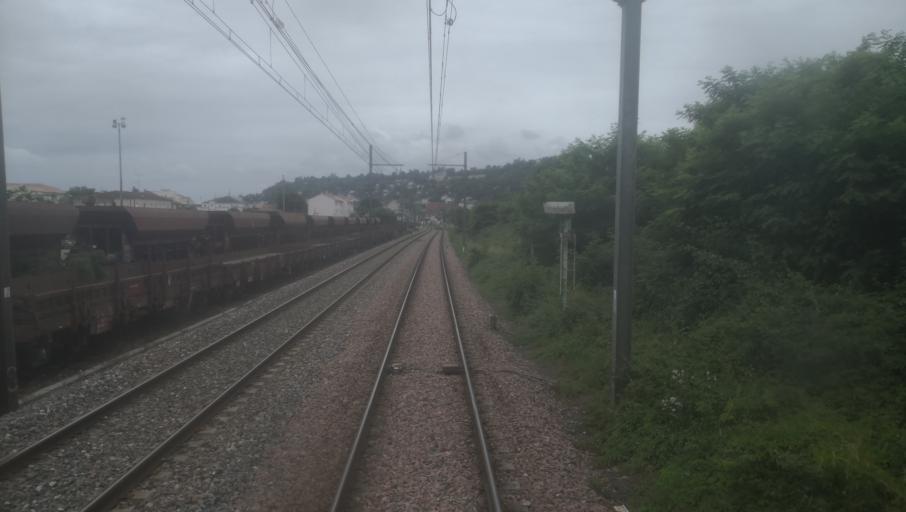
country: FR
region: Aquitaine
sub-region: Departement du Lot-et-Garonne
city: Agen
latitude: 44.2039
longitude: 0.6347
